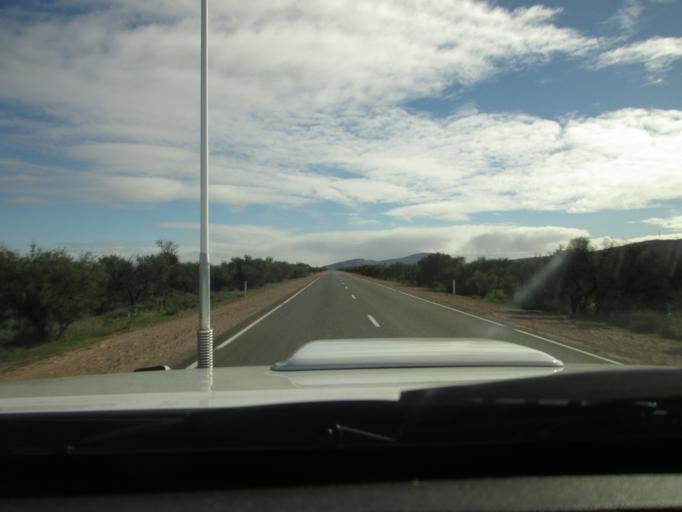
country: AU
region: South Australia
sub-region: Flinders Ranges
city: Quorn
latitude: -31.8551
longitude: 138.3994
